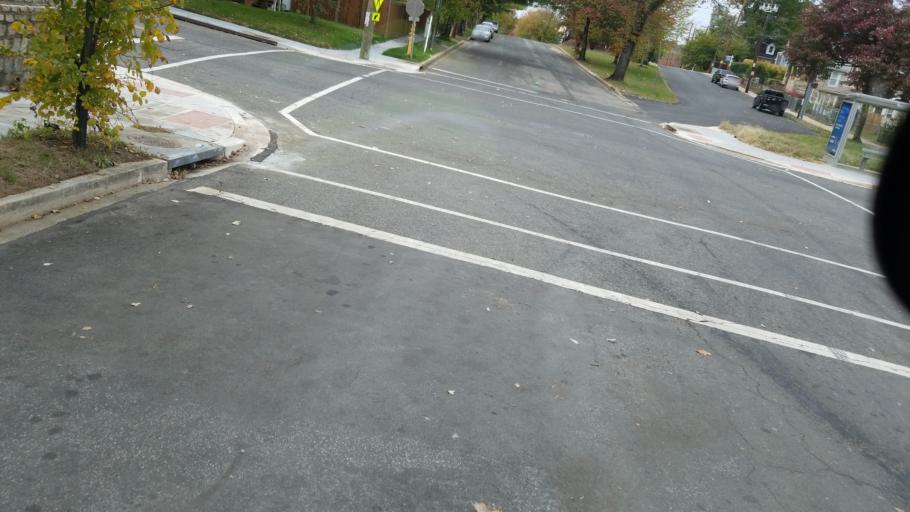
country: US
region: Maryland
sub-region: Prince George's County
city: Capitol Heights
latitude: 38.8919
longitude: -76.9277
